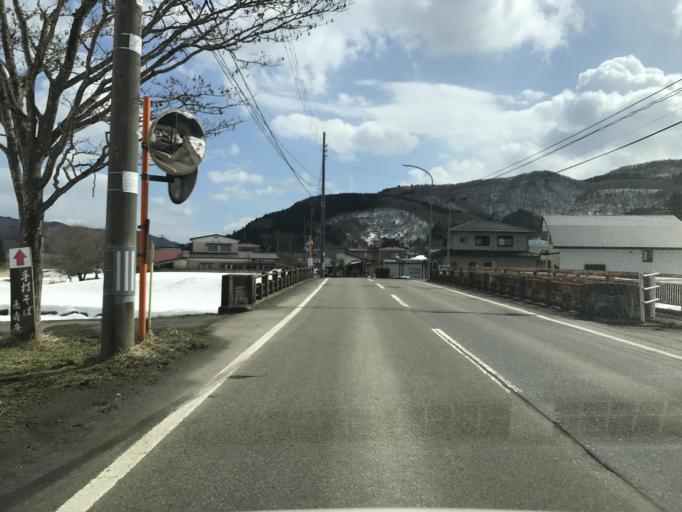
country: JP
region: Miyagi
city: Furukawa
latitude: 38.7317
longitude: 140.7587
